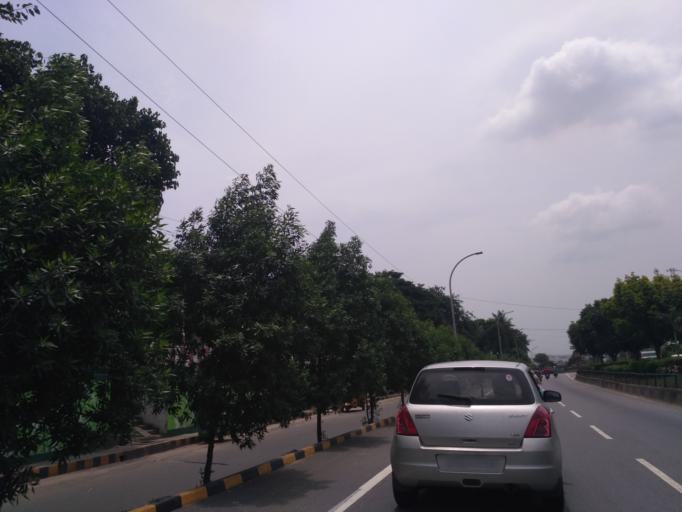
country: IN
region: Andhra Pradesh
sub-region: Vishakhapatnam
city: Gajuwaka
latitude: 17.7352
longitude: 83.2798
